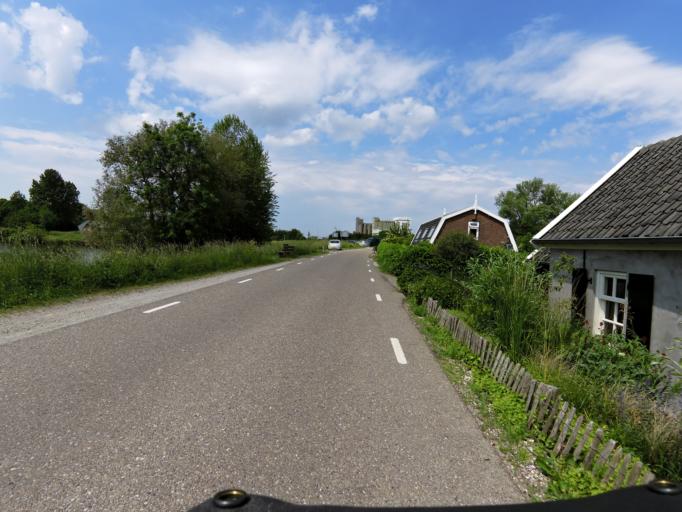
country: NL
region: North Brabant
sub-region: Gemeente Woudrichem
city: Woudrichem
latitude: 51.7937
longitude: 5.0548
